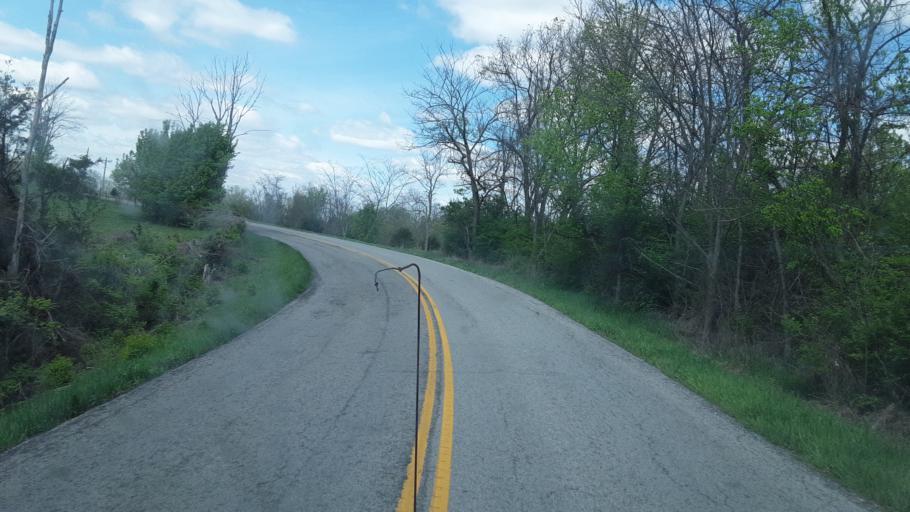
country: US
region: Kentucky
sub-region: Grant County
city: Dry Ridge
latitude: 38.6611
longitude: -84.6964
